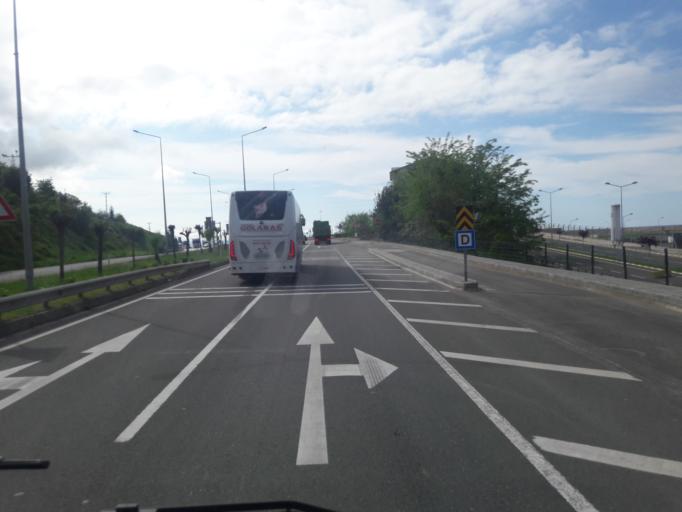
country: TR
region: Ordu
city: Gulyali
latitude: 40.9637
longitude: 38.0765
